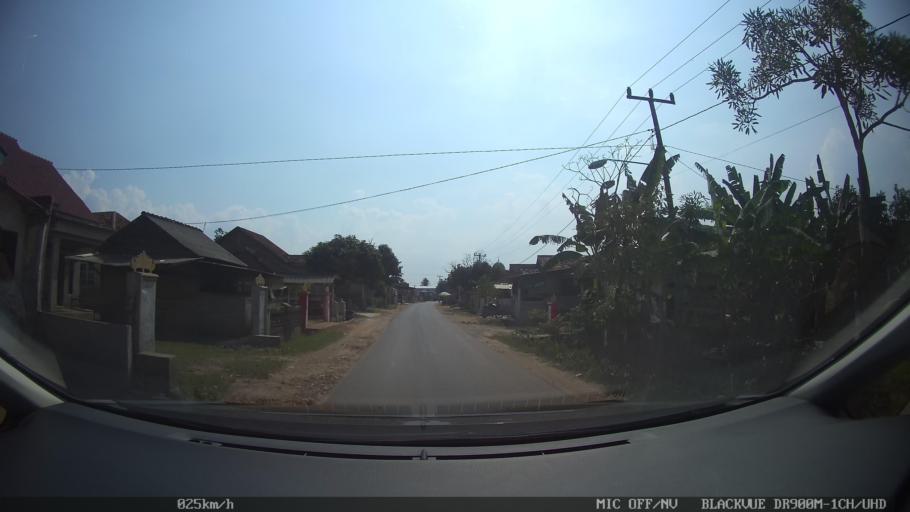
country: ID
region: Lampung
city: Natar
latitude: -5.3072
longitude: 105.2194
